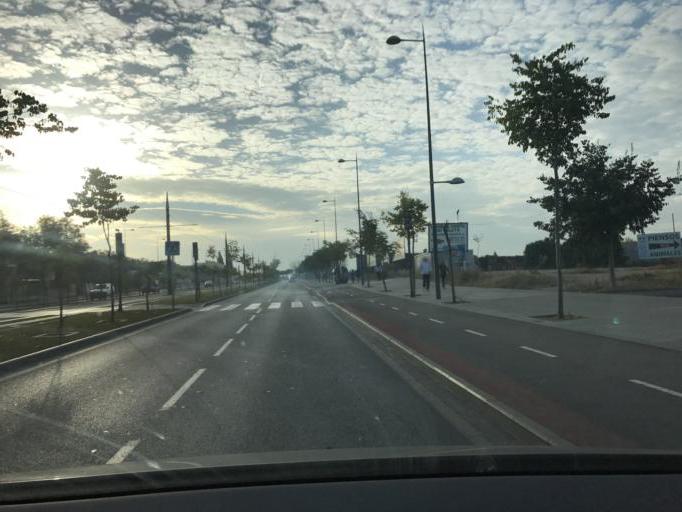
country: ES
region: Andalusia
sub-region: Provincia de Granada
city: Maracena
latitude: 37.2178
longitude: -3.6421
